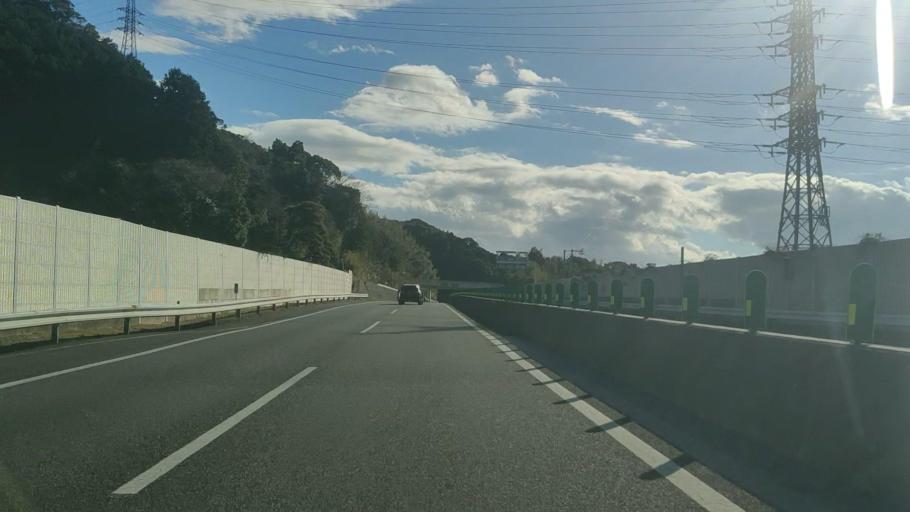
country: JP
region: Fukuoka
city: Kitakyushu
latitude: 33.8358
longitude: 130.7656
